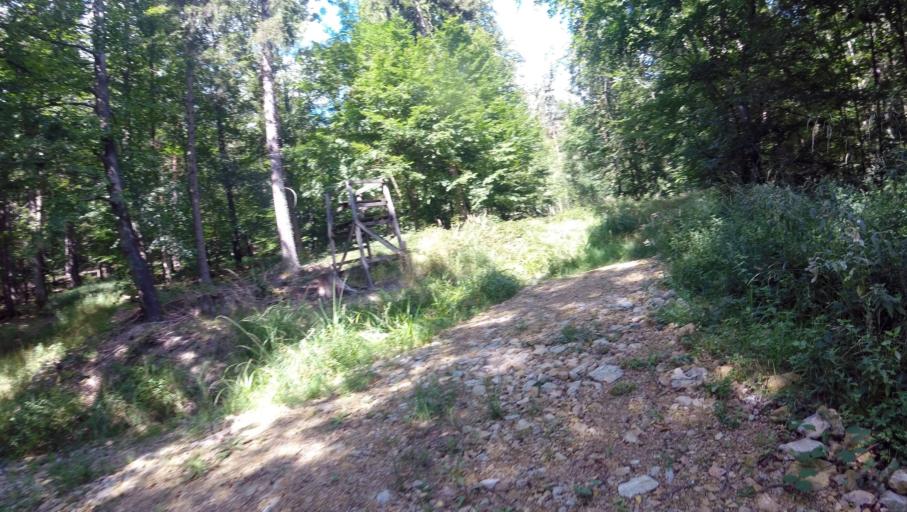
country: DE
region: Baden-Wuerttemberg
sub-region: Regierungsbezirk Stuttgart
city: Spiegelberg
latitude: 49.0070
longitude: 9.4230
